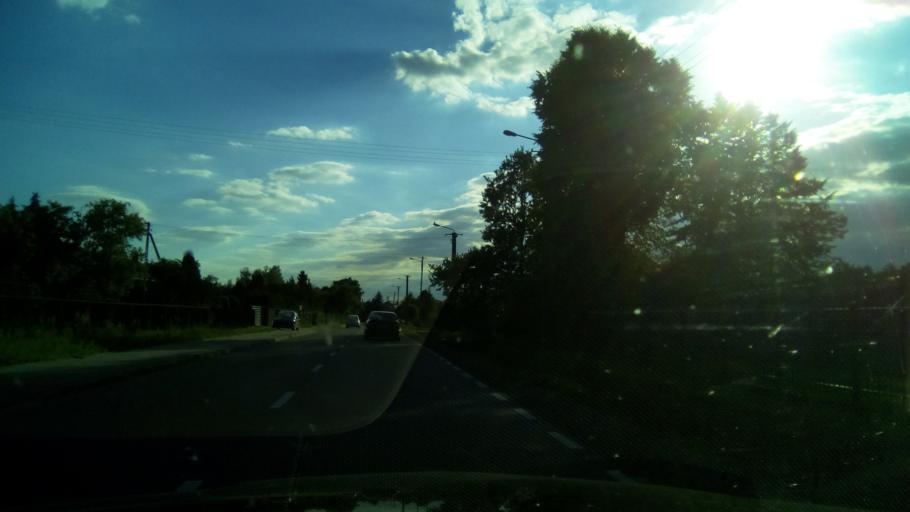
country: PL
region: Masovian Voivodeship
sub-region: Powiat bialobrzeski
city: Stromiec
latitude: 51.6471
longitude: 21.0965
